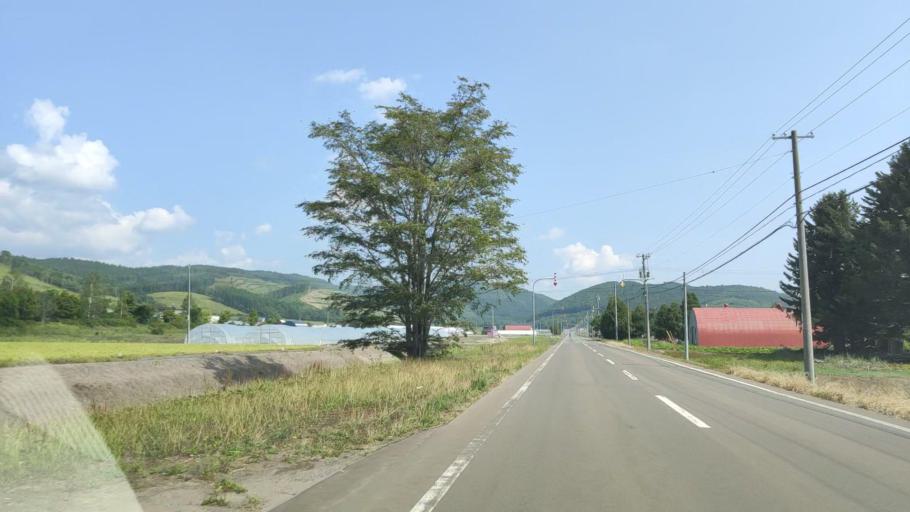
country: JP
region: Hokkaido
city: Shimo-furano
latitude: 43.4078
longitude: 142.3966
